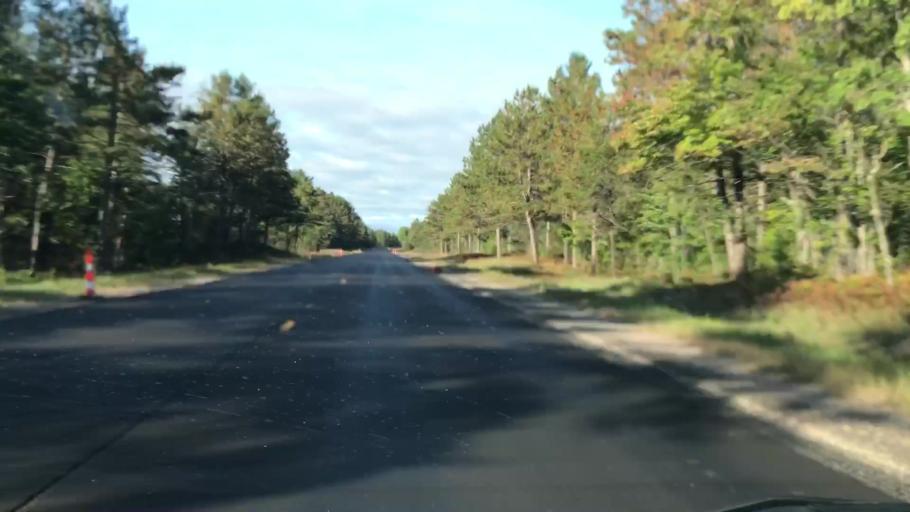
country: US
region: Michigan
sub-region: Mackinac County
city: Saint Ignace
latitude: 46.3508
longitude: -84.9079
